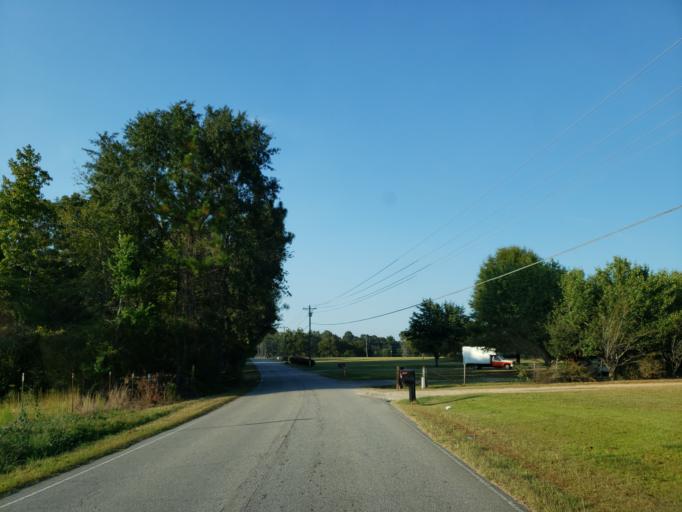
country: US
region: Mississippi
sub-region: Lamar County
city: West Hattiesburg
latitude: 31.3317
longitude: -89.4466
